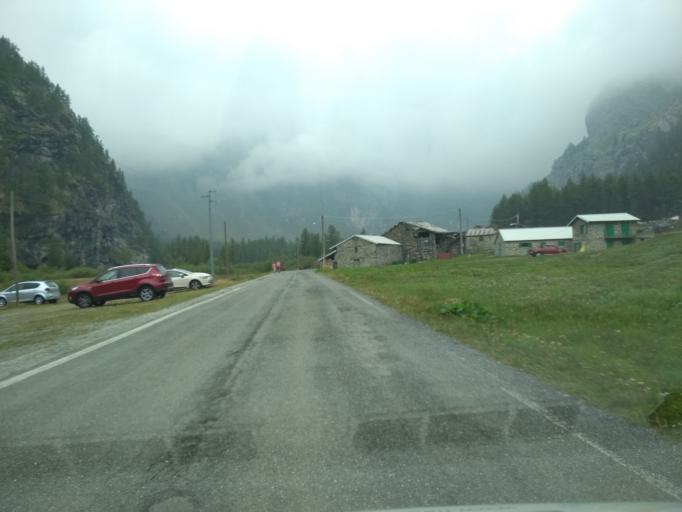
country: IT
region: Piedmont
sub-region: Provincia di Torino
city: Balme
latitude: 45.3033
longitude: 7.1786
